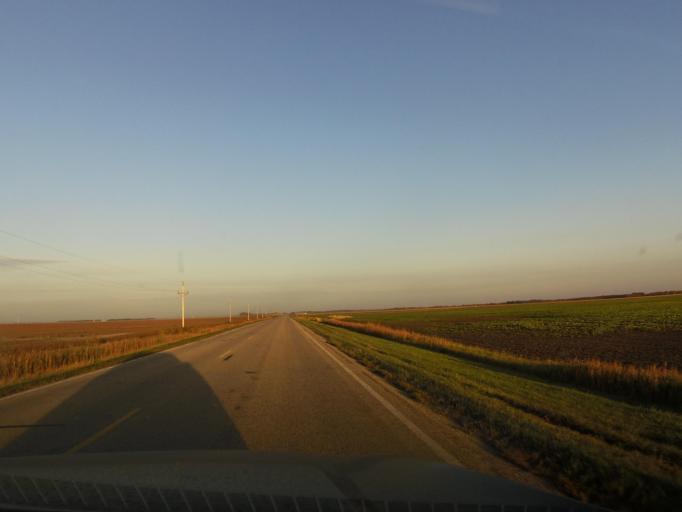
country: CA
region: Manitoba
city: Altona
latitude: 48.9632
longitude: -97.3344
